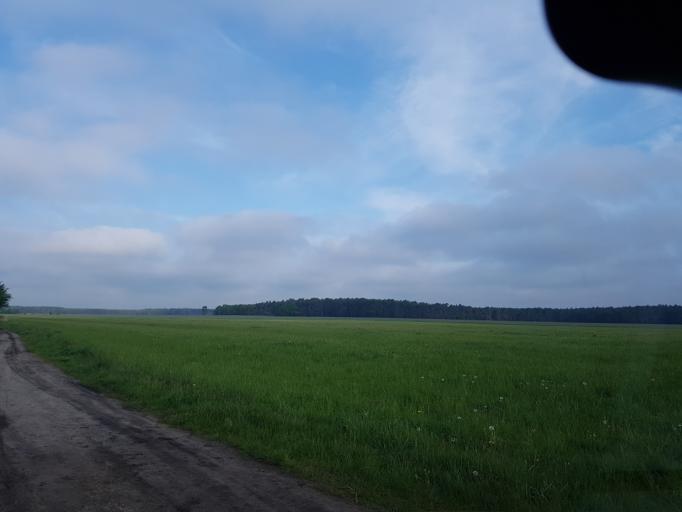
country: DE
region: Brandenburg
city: Finsterwalde
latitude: 51.5709
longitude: 13.6709
